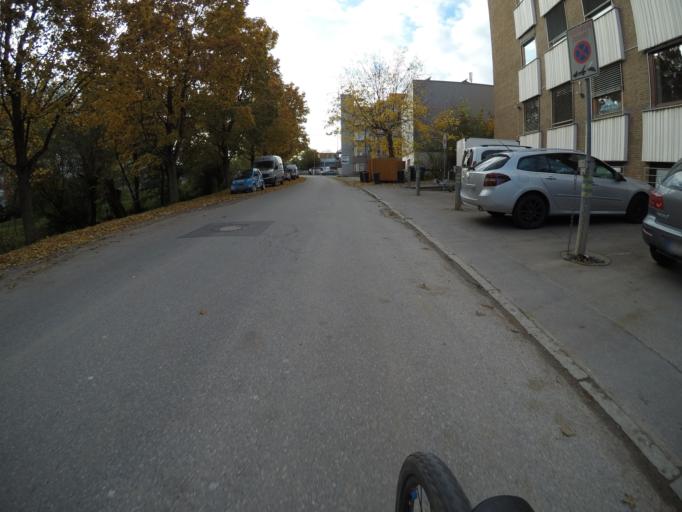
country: DE
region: Baden-Wuerttemberg
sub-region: Regierungsbezirk Stuttgart
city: Filderstadt
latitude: 48.6770
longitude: 9.1998
